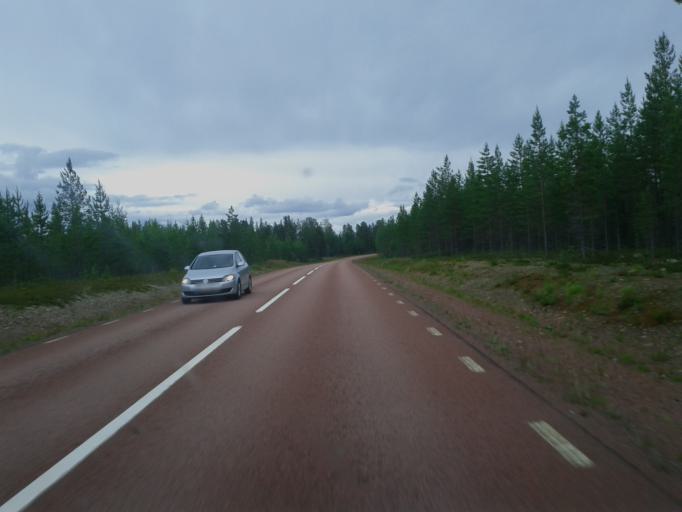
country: SE
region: Dalarna
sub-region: Alvdalens Kommun
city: AElvdalen
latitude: 61.5490
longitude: 13.3311
